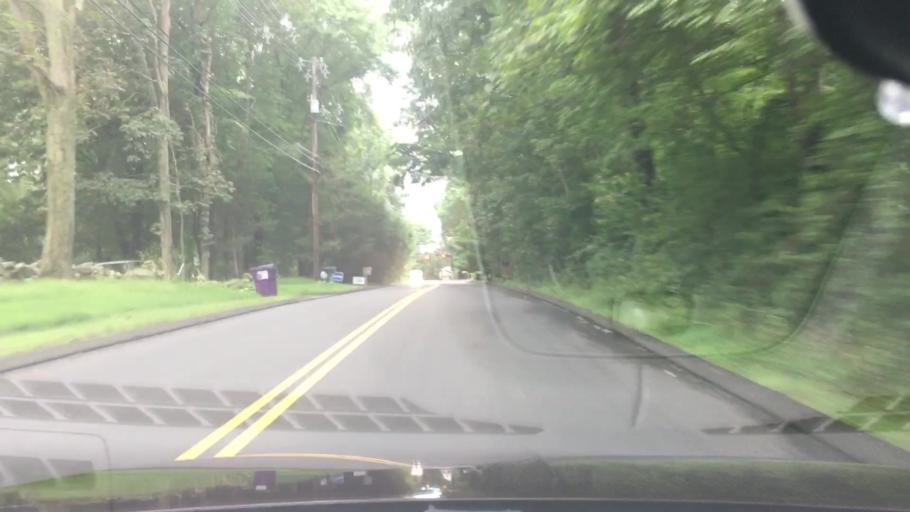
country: US
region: Connecticut
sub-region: New Haven County
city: Madison
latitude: 41.3137
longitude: -72.5953
